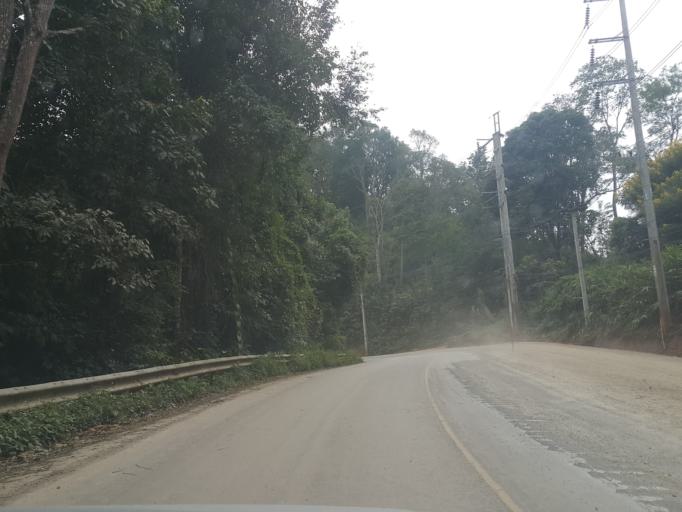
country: TH
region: Chiang Mai
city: Mae Taeng
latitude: 19.1209
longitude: 98.7147
